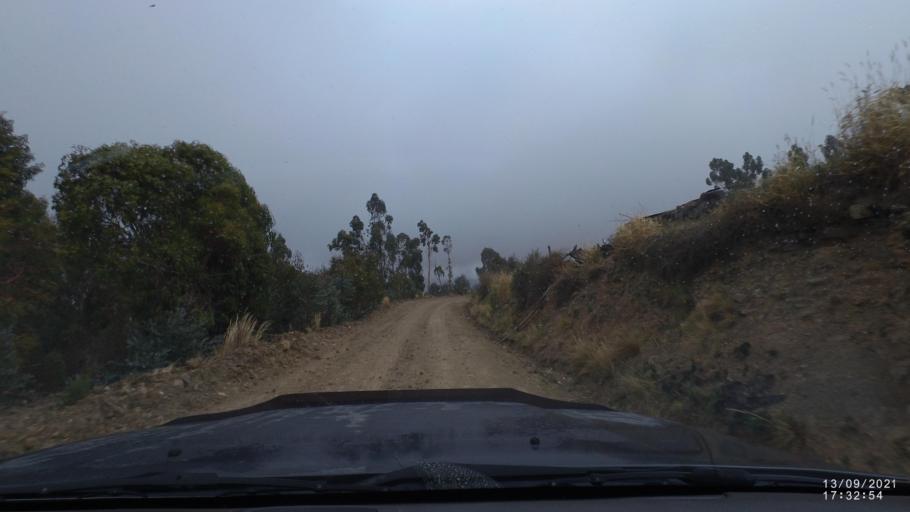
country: BO
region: Cochabamba
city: Colomi
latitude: -17.3674
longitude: -65.7899
